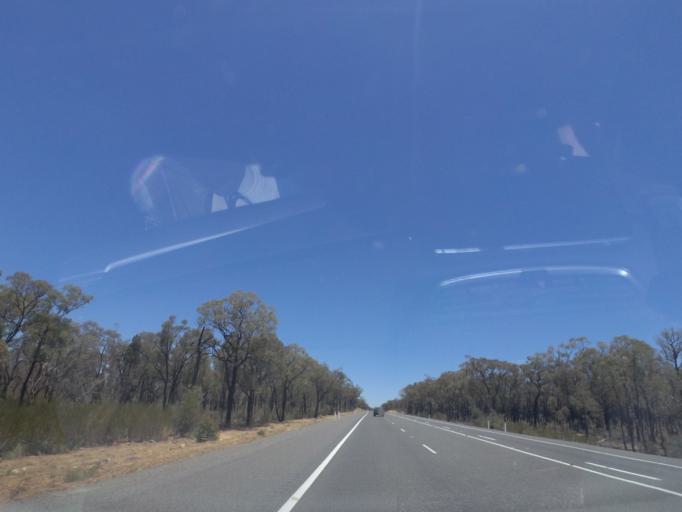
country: AU
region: New South Wales
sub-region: Warrumbungle Shire
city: Coonabarabran
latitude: -30.8987
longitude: 149.4400
